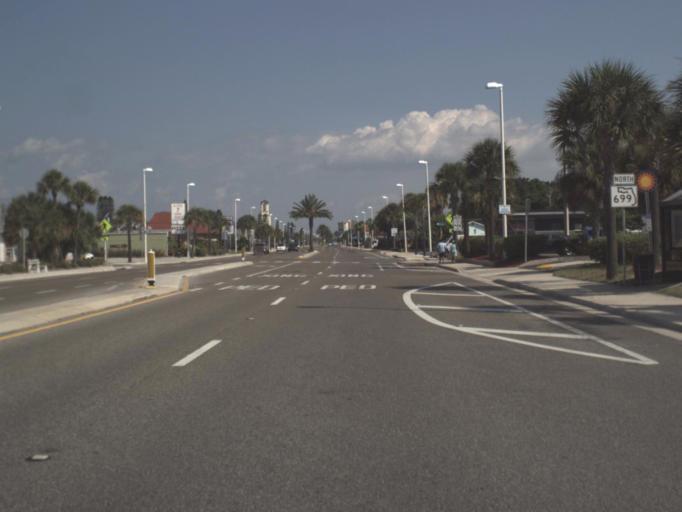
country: US
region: Florida
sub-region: Pinellas County
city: South Pasadena
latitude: 27.7435
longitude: -82.7508
